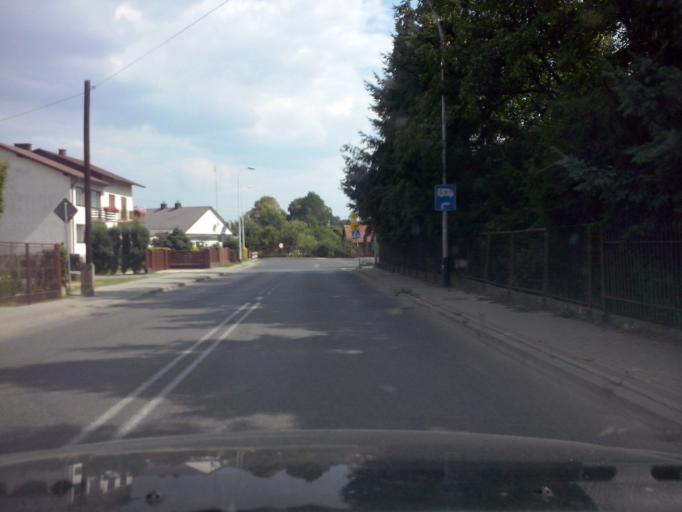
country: PL
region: Subcarpathian Voivodeship
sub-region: Powiat nizanski
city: Nisko
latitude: 50.5187
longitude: 22.1354
